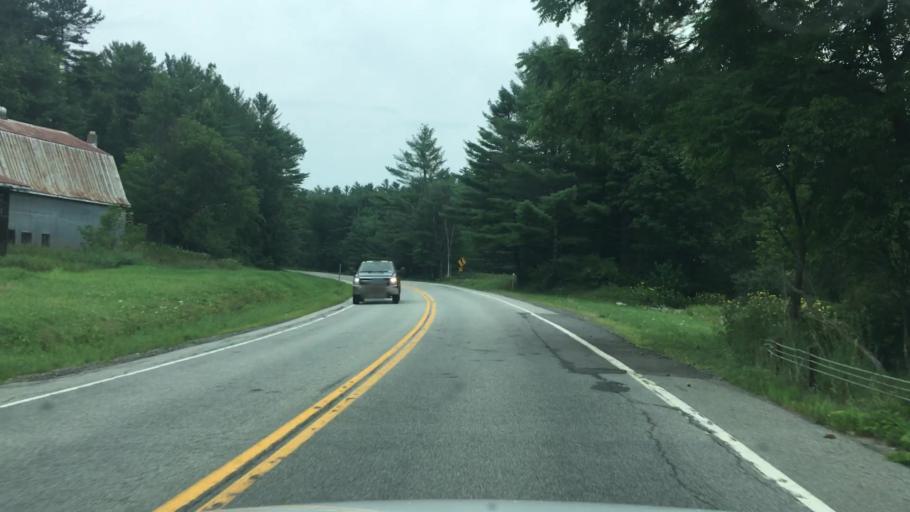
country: US
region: New York
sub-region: Essex County
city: Keeseville
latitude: 44.4168
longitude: -73.6799
